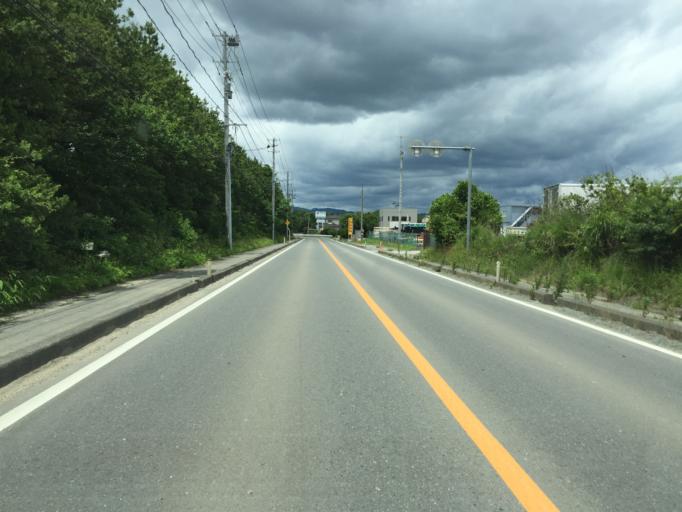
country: JP
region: Fukushima
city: Namie
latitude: 37.6196
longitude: 140.9932
